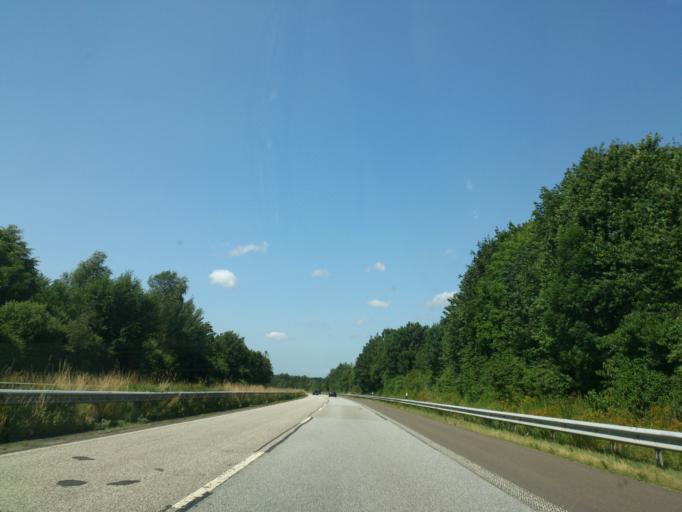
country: DE
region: Schleswig-Holstein
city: Nordhastedt
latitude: 54.1619
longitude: 9.2097
